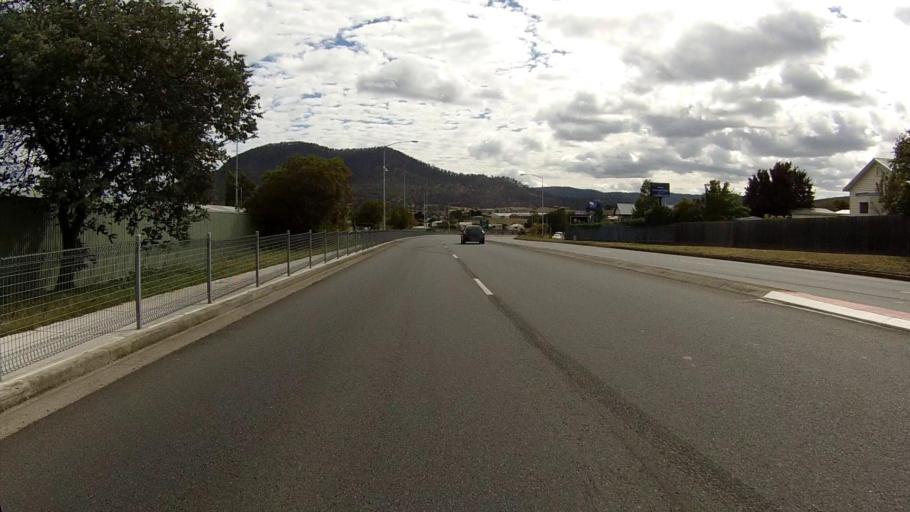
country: AU
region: Tasmania
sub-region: Glenorchy
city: Goodwood
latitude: -42.8255
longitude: 147.2898
